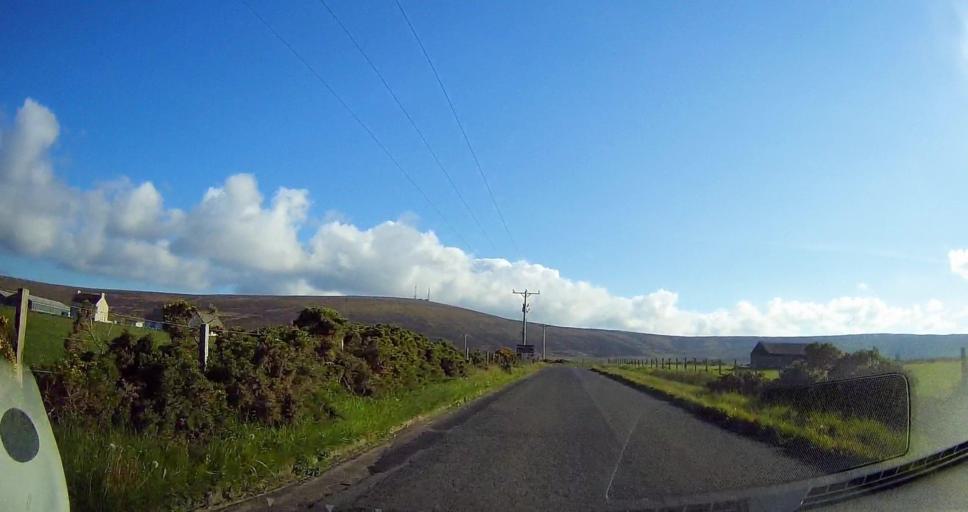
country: GB
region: Scotland
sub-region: Orkney Islands
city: Orkney
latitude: 58.9932
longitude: -3.0720
